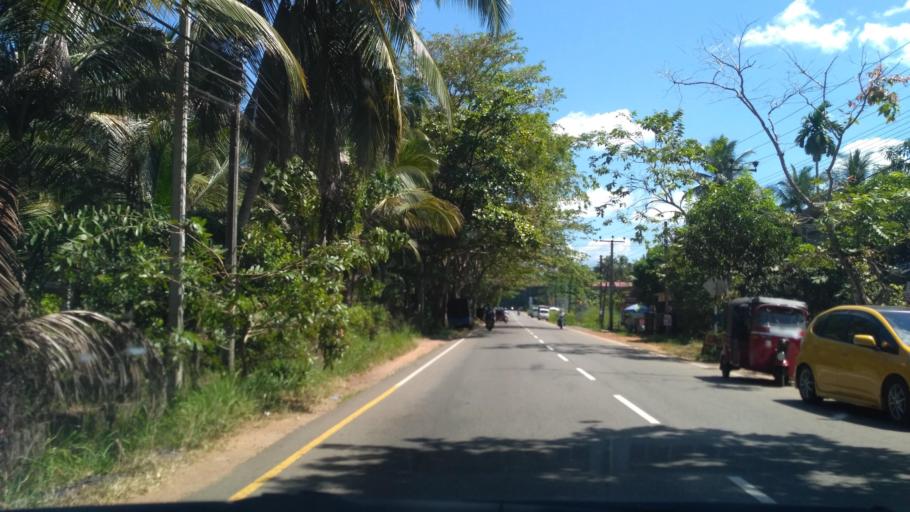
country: LK
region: North Western
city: Kuliyapitiya
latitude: 7.3239
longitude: 80.0982
